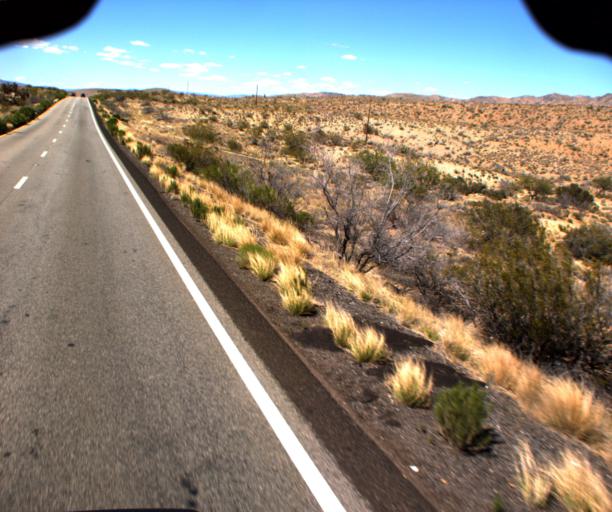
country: US
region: Arizona
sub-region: Mohave County
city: Kingman
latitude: 34.9802
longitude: -113.6680
